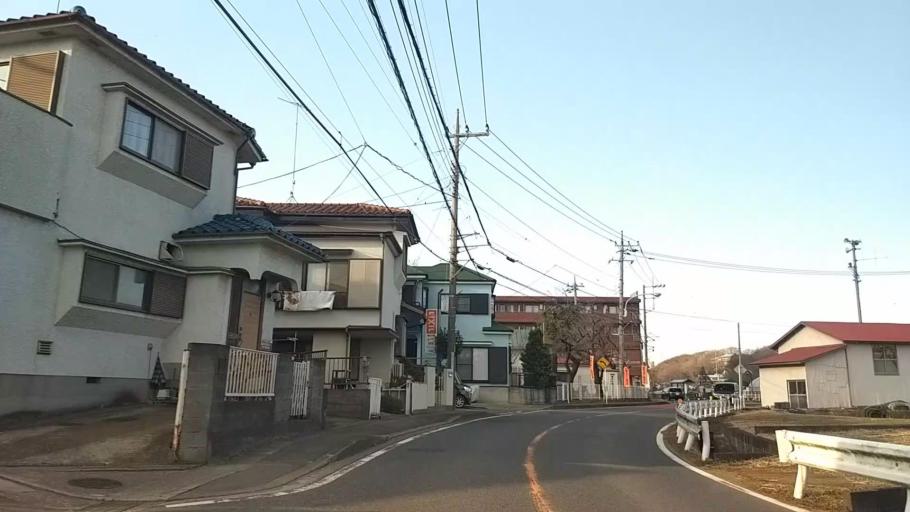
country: JP
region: Kanagawa
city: Atsugi
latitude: 35.4422
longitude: 139.3354
